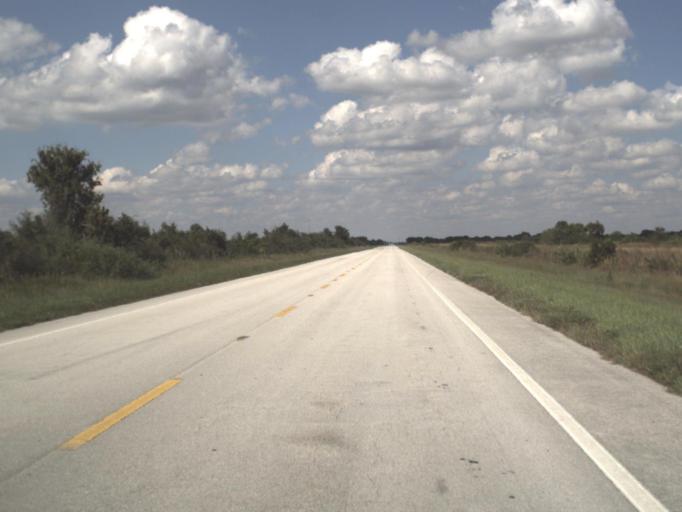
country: US
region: Florida
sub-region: Highlands County
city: Lake Placid
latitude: 27.4084
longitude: -81.1807
